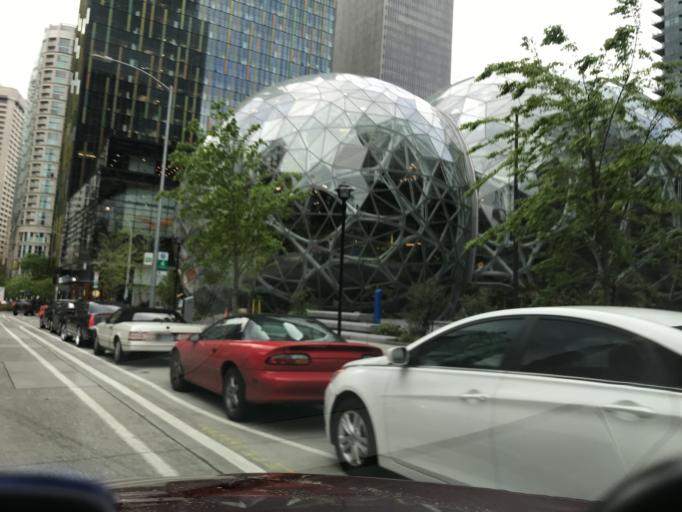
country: US
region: Washington
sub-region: King County
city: Seattle
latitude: 47.6163
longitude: -122.3396
